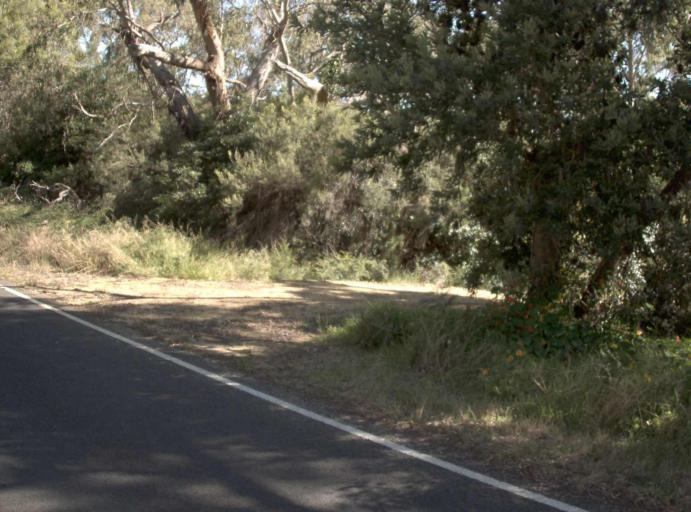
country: AU
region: Victoria
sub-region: Latrobe
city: Traralgon
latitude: -38.6549
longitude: 146.6779
